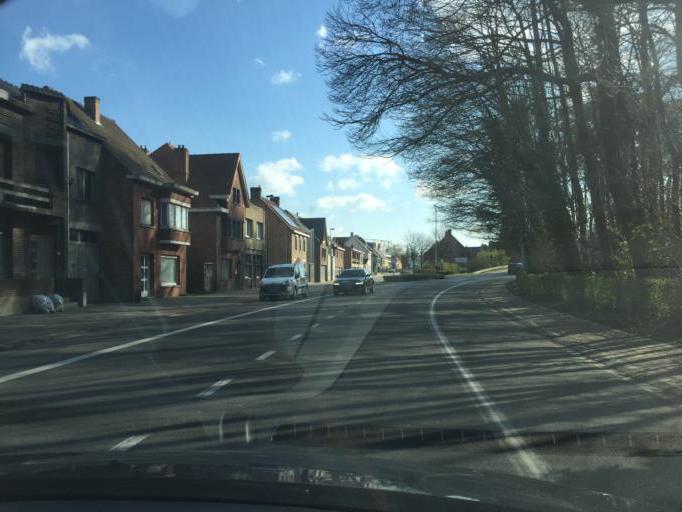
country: BE
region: Flanders
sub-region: Provincie West-Vlaanderen
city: Beernem
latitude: 51.1303
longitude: 3.3308
